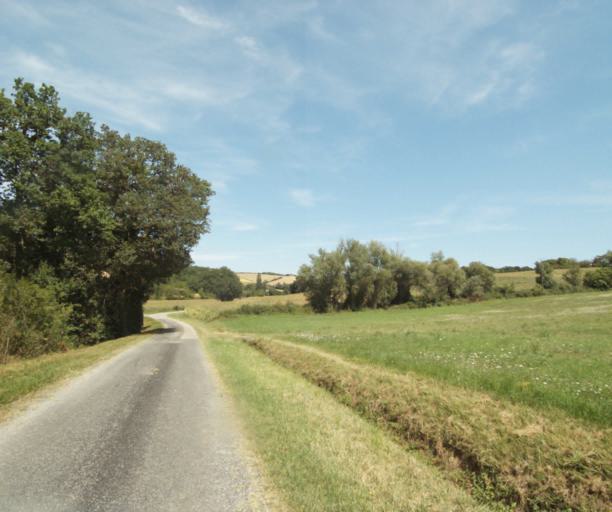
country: FR
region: Midi-Pyrenees
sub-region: Departement de l'Ariege
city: Lezat-sur-Leze
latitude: 43.2519
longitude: 1.3770
